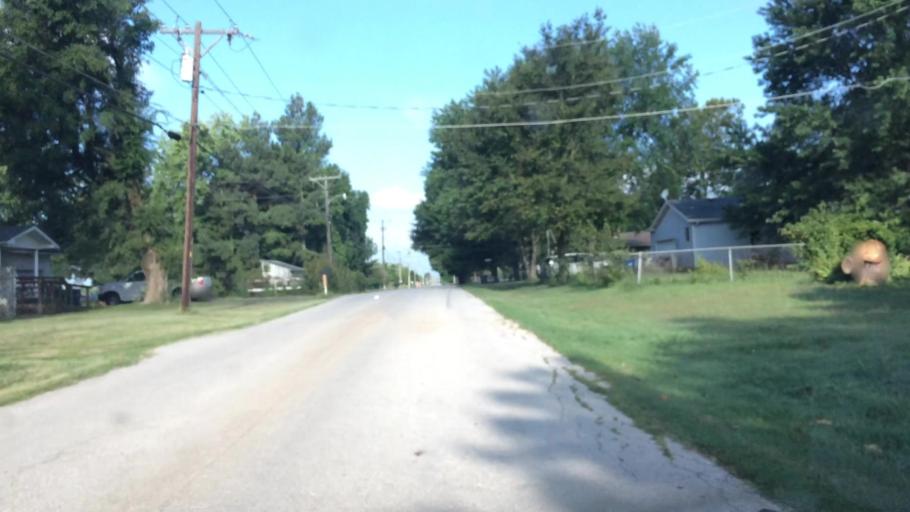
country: US
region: Missouri
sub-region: Greene County
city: Strafford
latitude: 37.2708
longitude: -93.1293
